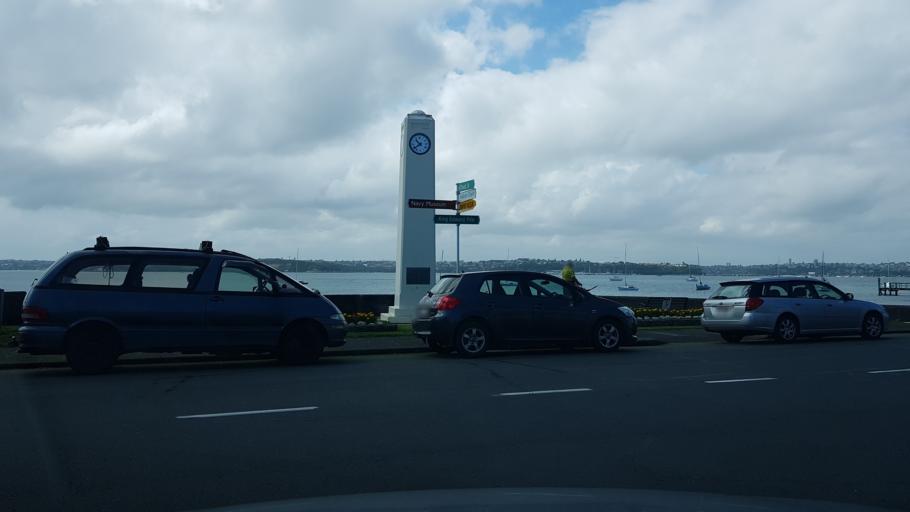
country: NZ
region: Auckland
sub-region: Auckland
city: Auckland
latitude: -36.8298
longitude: 174.8039
